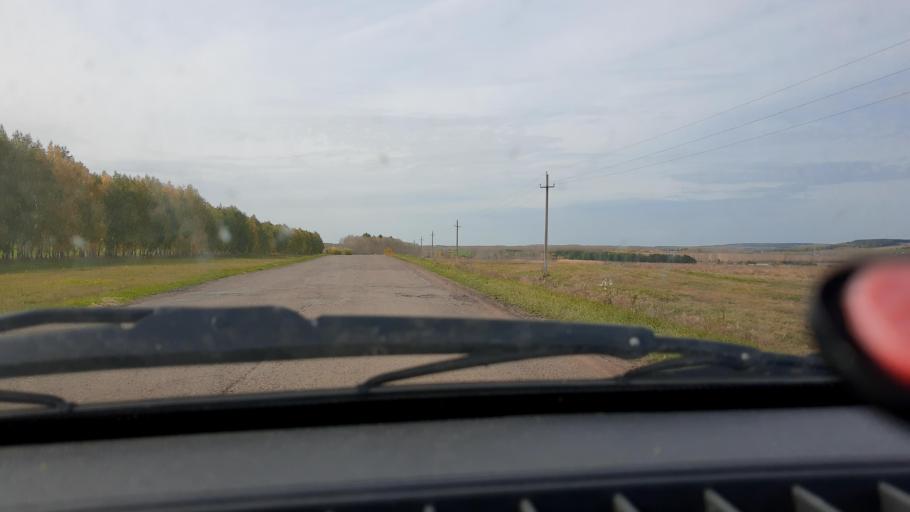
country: RU
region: Bashkortostan
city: Chekmagush
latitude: 54.8841
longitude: 54.5972
